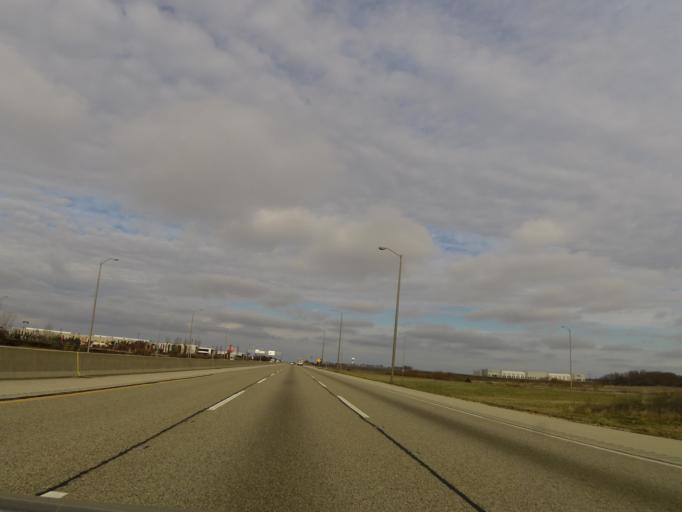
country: US
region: Illinois
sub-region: Winnebago County
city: Machesney Park
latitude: 42.3200
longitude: -88.9646
